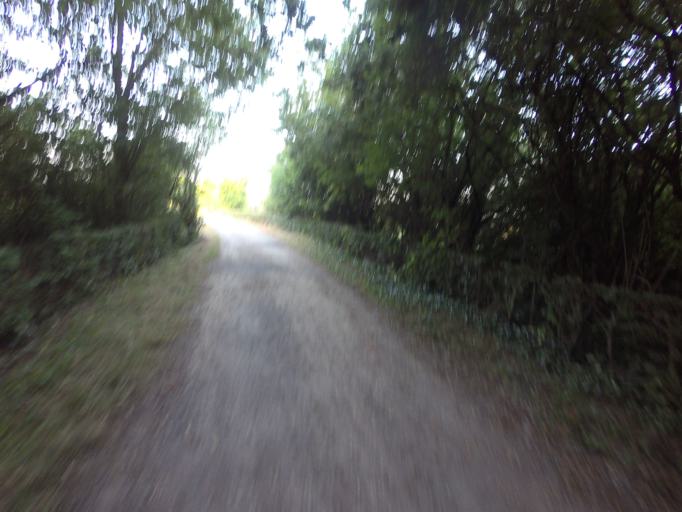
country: NL
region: Limburg
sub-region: Valkenburg aan de Geul
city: Schin op Geul
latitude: 50.7941
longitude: 5.8917
